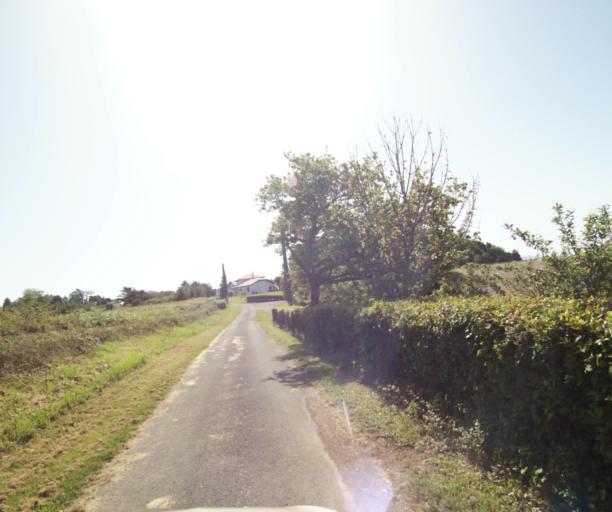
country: FR
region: Aquitaine
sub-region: Departement des Pyrenees-Atlantiques
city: Villefranque
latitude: 43.4531
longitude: -1.4482
